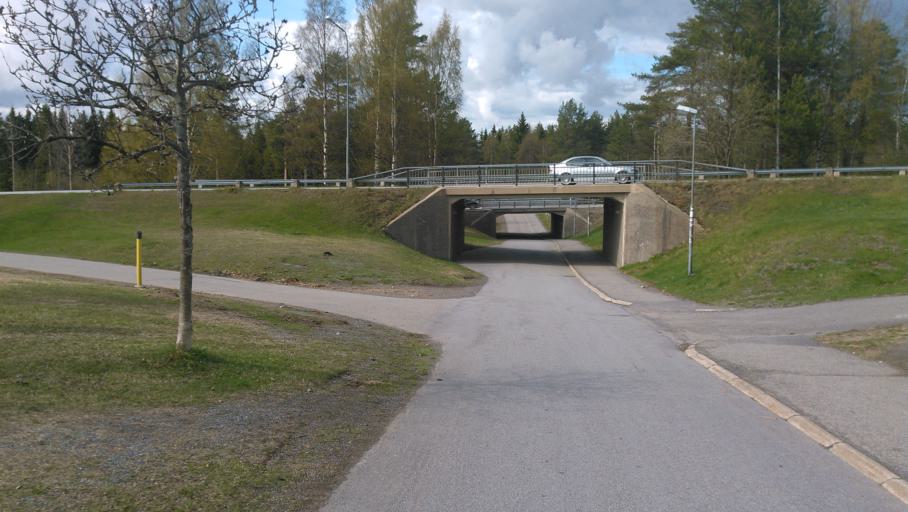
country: SE
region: Vaesterbotten
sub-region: Umea Kommun
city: Umea
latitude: 63.8036
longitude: 20.3185
